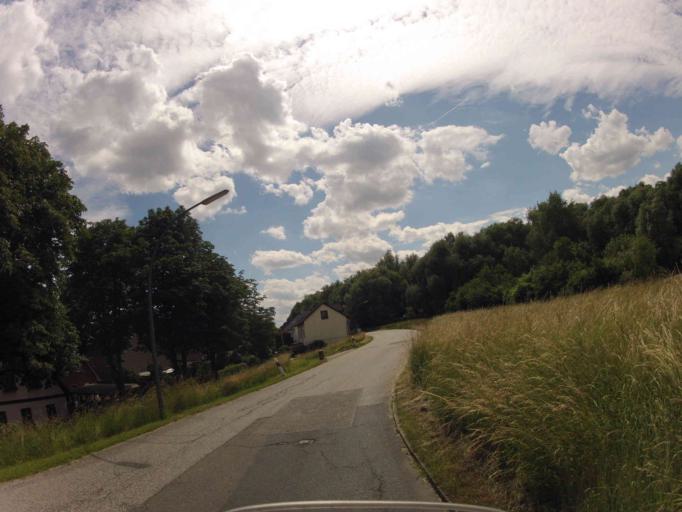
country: DE
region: Hamburg
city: Rothenburgsort
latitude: 53.5104
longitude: 10.0751
